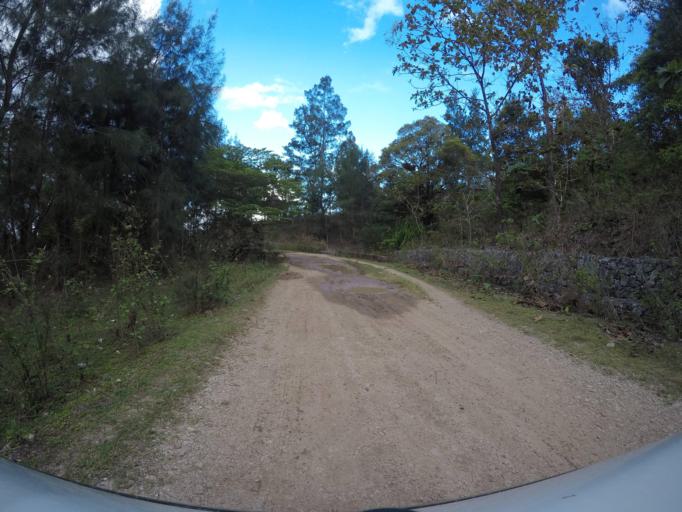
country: TL
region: Baucau
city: Venilale
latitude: -8.6872
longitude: 126.6596
